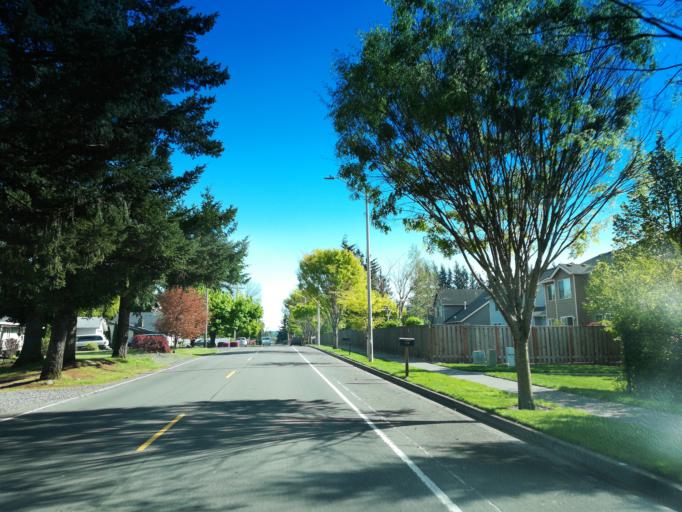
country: US
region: Oregon
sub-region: Multnomah County
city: Troutdale
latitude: 45.5299
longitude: -122.3934
